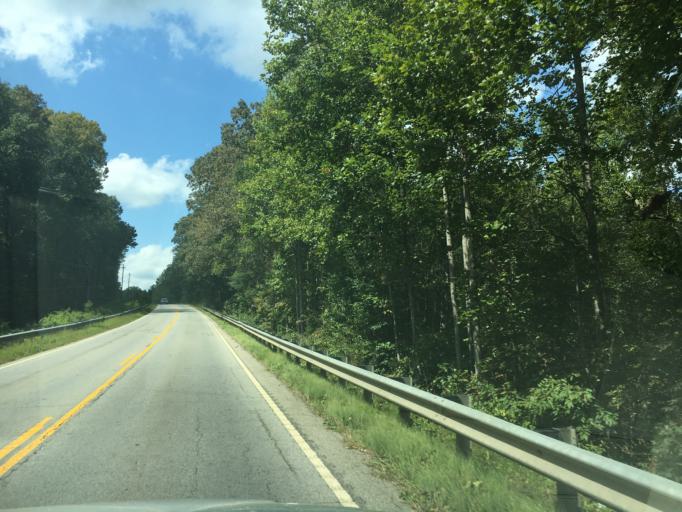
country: US
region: South Carolina
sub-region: Greenville County
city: Berea
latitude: 34.8866
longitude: -82.5045
